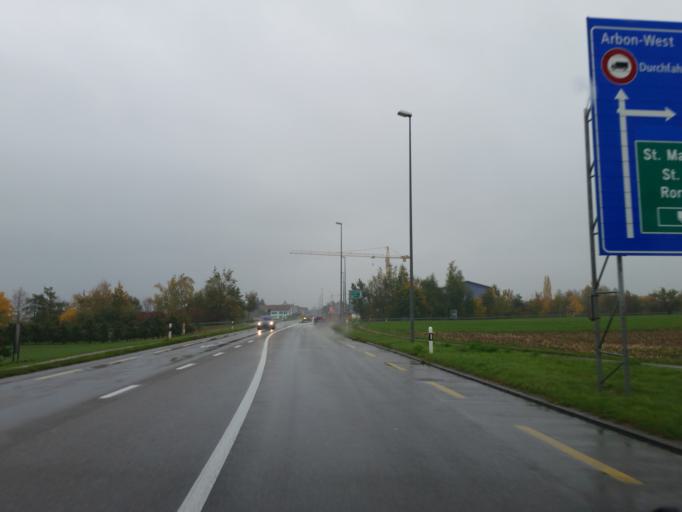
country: CH
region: Thurgau
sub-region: Arbon District
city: Roggwil
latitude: 47.5236
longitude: 9.3962
